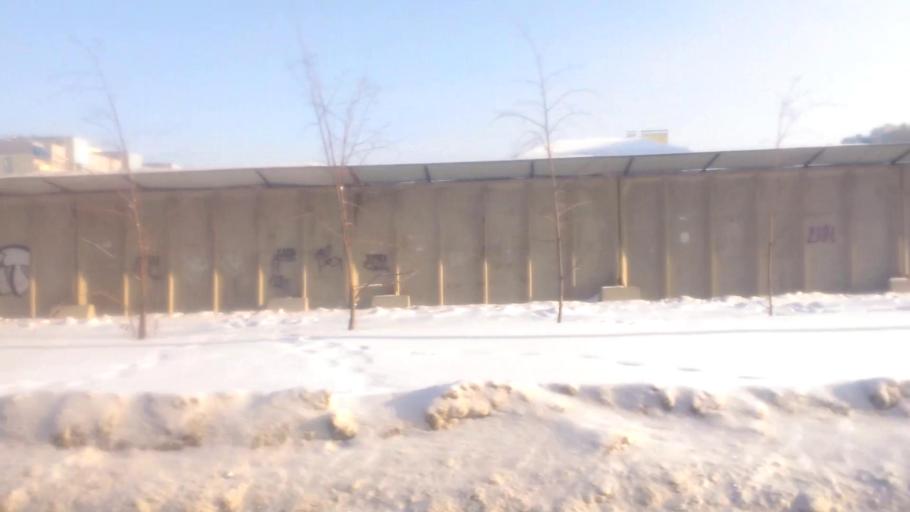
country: RU
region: Altai Krai
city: Novosilikatnyy
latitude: 53.3429
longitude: 83.6554
